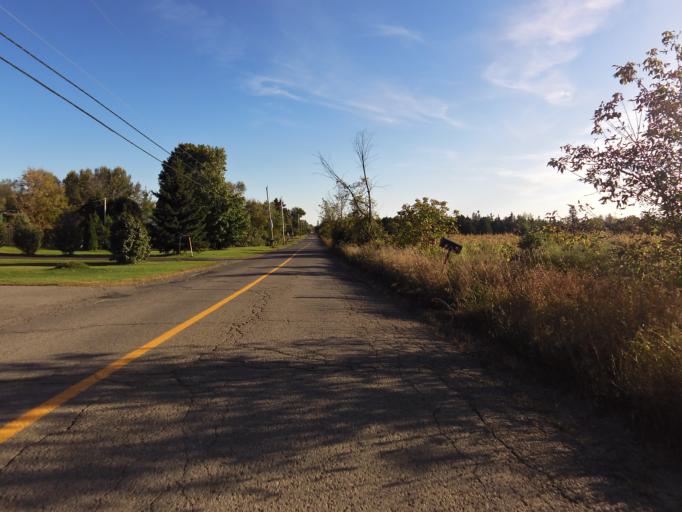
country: CA
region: Ontario
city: Bells Corners
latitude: 45.4336
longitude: -75.8798
